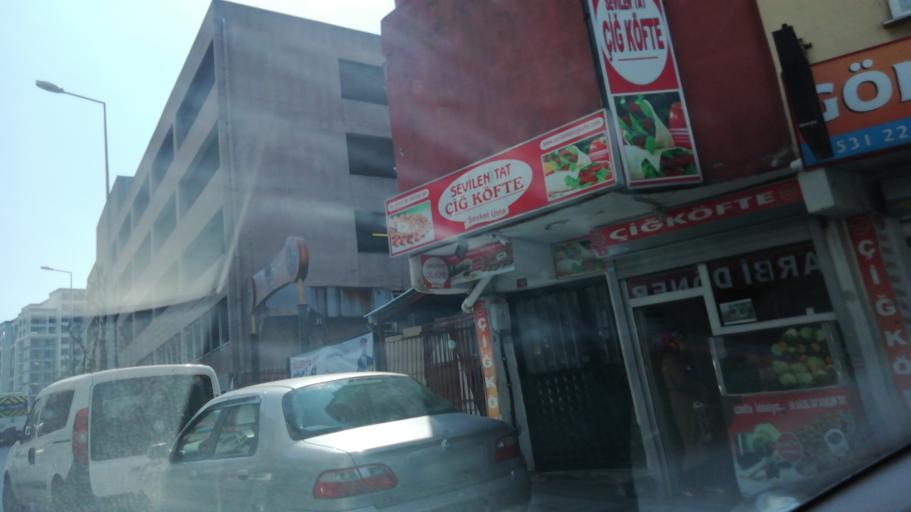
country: TR
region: Istanbul
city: Mahmutbey
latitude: 41.0331
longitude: 28.8202
